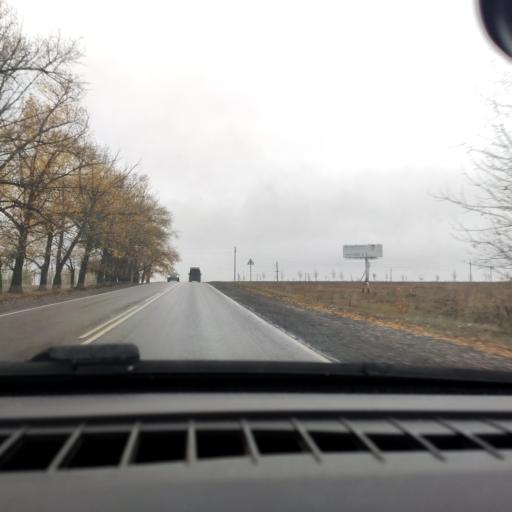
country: RU
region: Belgorod
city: Ilovka
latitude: 50.6951
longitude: 38.6588
